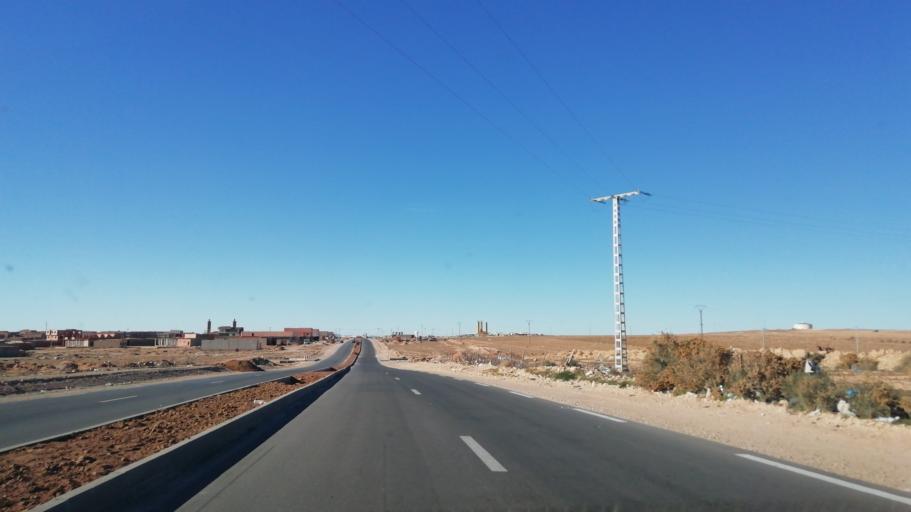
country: DZ
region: Tlemcen
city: Sebdou
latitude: 34.2141
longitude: -1.2436
